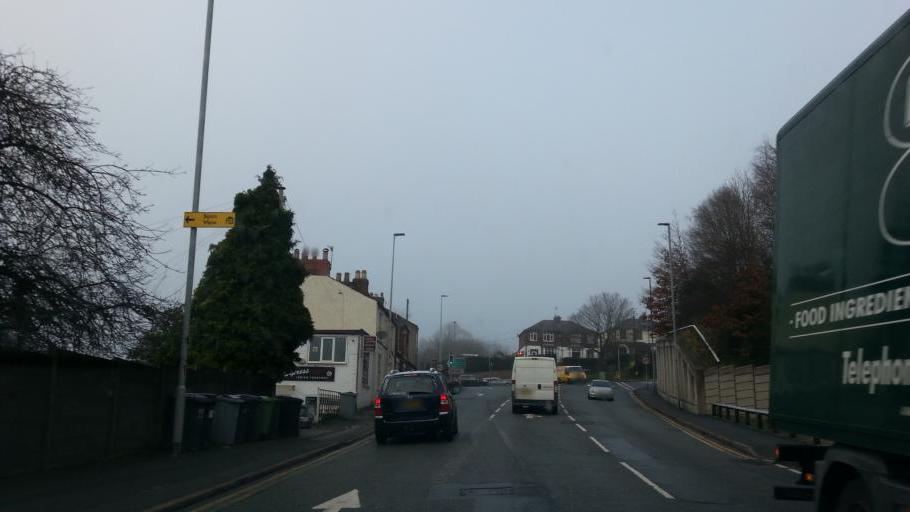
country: GB
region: England
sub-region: Cheshire East
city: Congleton
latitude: 53.1679
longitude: -2.2145
